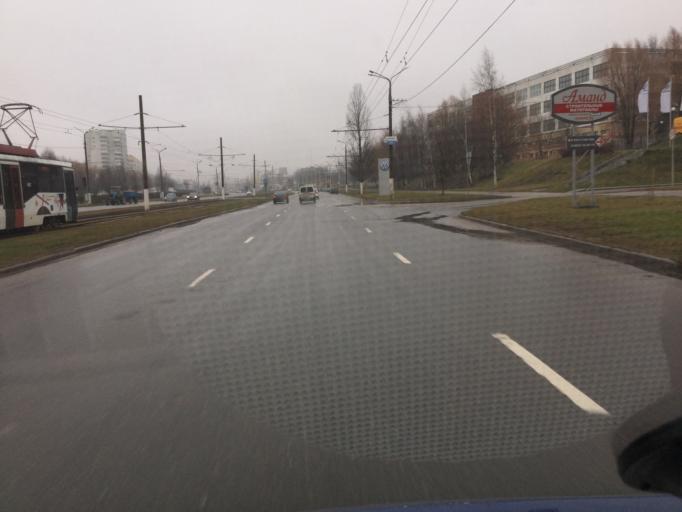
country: BY
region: Vitebsk
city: Vitebsk
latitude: 55.1646
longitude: 30.2395
